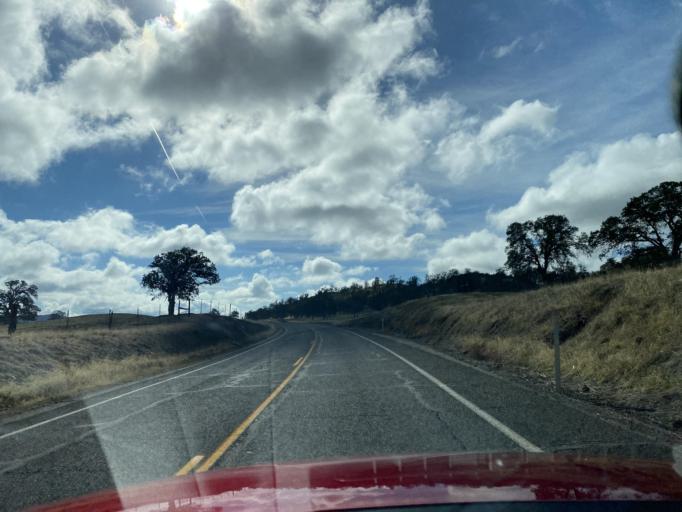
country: US
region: California
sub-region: Glenn County
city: Willows
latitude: 39.5396
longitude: -122.5354
